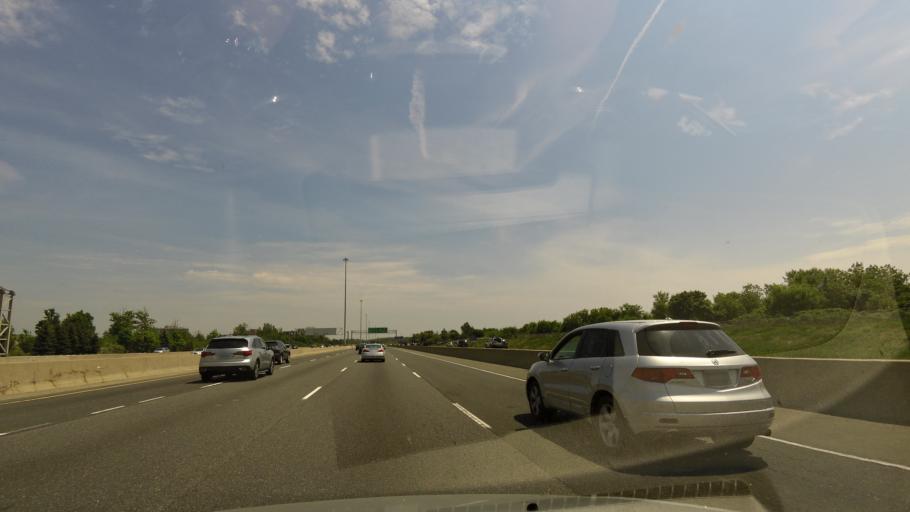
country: CA
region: Ontario
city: Scarborough
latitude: 43.7984
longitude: -79.1826
